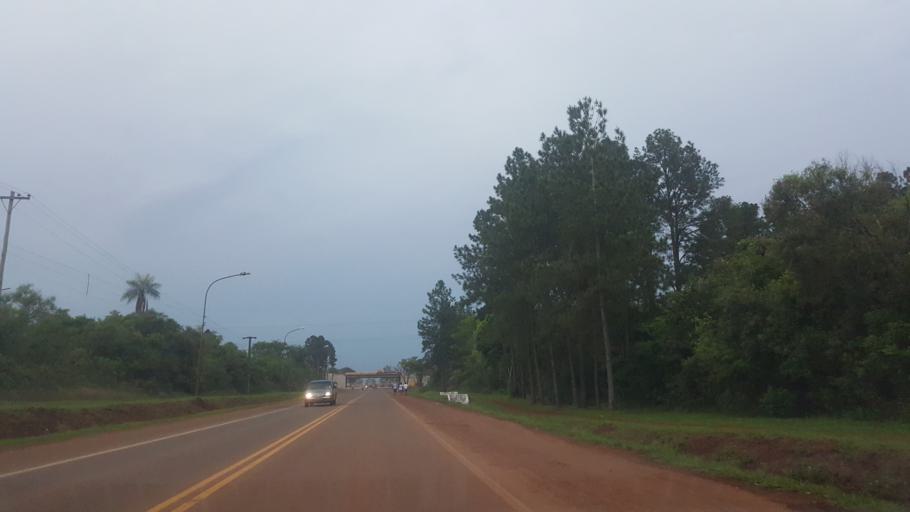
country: AR
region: Misiones
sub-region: Departamento de Candelaria
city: Candelaria
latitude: -27.4746
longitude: -55.7463
